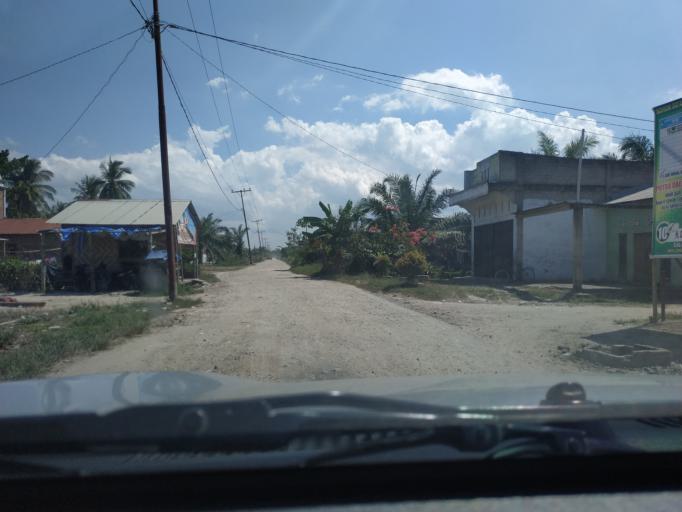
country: ID
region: North Sumatra
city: Tanjungbalai
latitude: 2.8845
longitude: 99.8616
